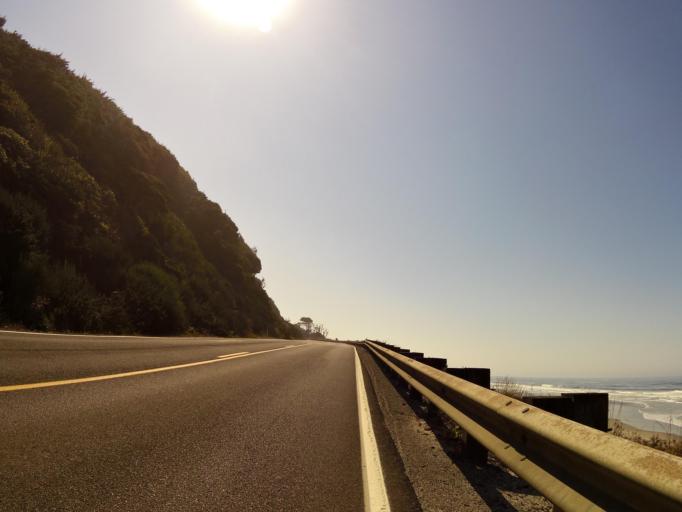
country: US
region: Oregon
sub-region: Tillamook County
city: Pacific City
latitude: 45.2410
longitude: -123.9690
